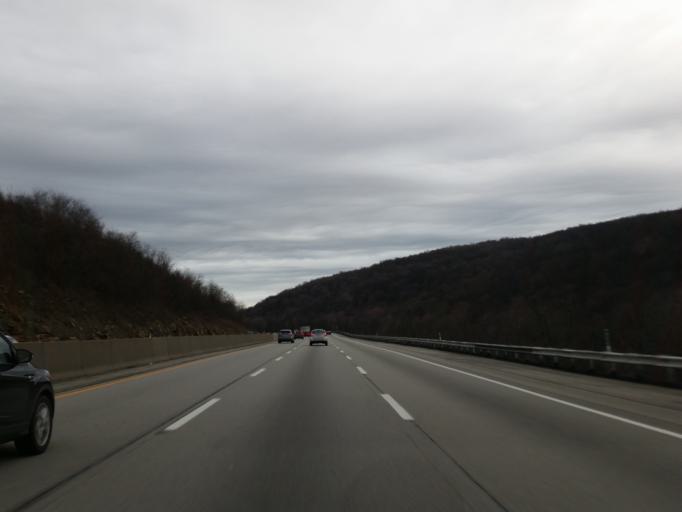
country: US
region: Pennsylvania
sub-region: Westmoreland County
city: Ligonier
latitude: 40.1163
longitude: -79.2605
